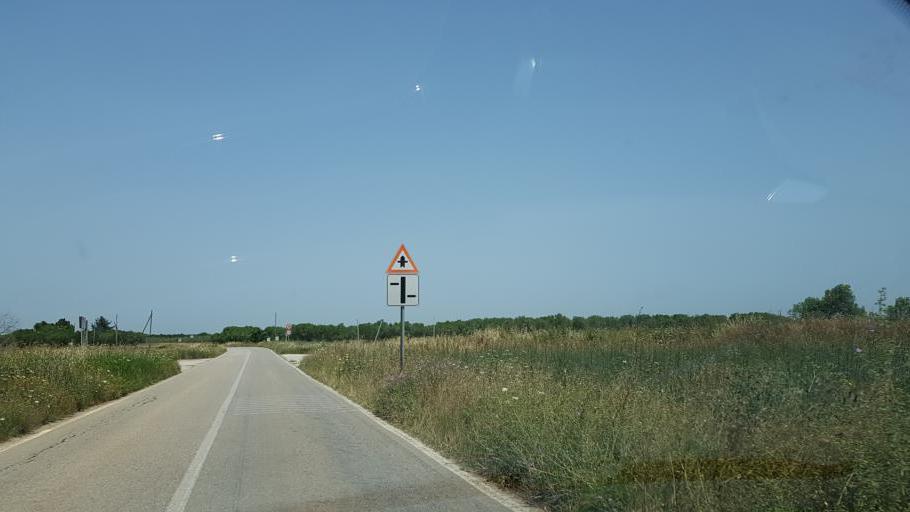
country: IT
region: Apulia
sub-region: Provincia di Brindisi
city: San Pancrazio Salentino
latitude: 40.4406
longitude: 17.8406
